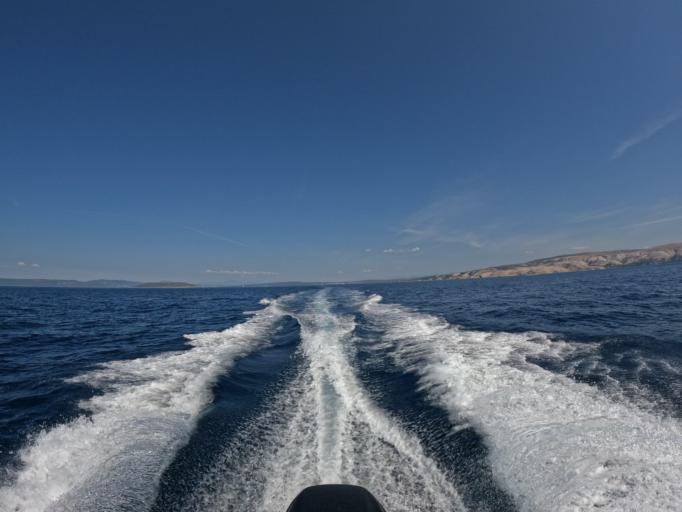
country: HR
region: Primorsko-Goranska
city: Punat
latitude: 44.9121
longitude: 14.6271
